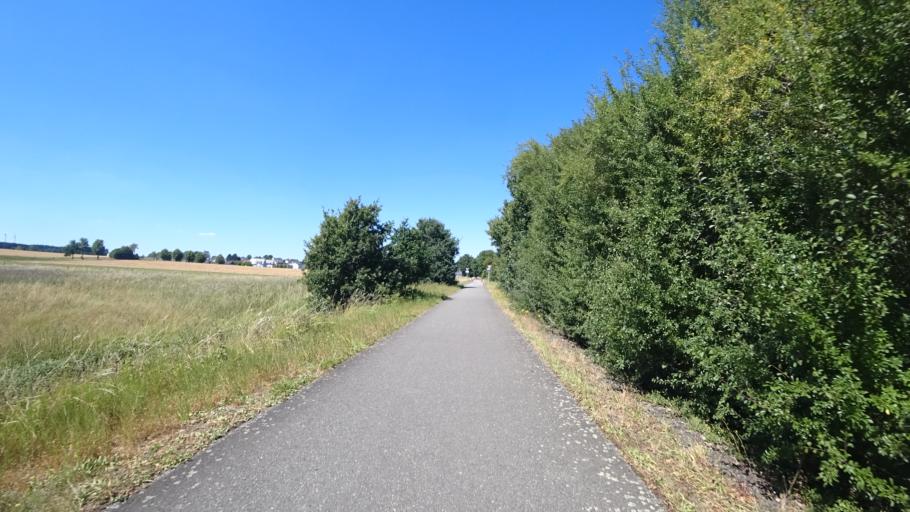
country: DE
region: Rheinland-Pfalz
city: Keidelheim
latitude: 50.0021
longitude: 7.4990
